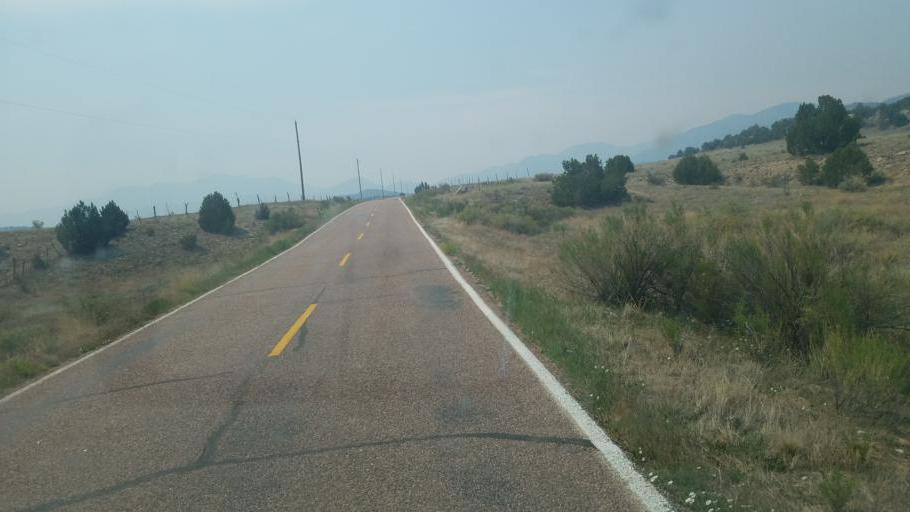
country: US
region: Colorado
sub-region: Fremont County
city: Canon City
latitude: 38.4678
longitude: -105.3776
